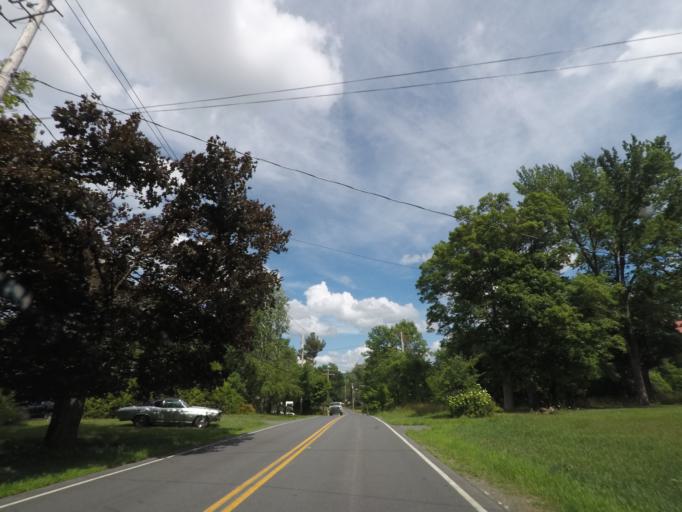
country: US
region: New York
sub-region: Rensselaer County
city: Wynantskill
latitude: 42.7268
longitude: -73.6110
